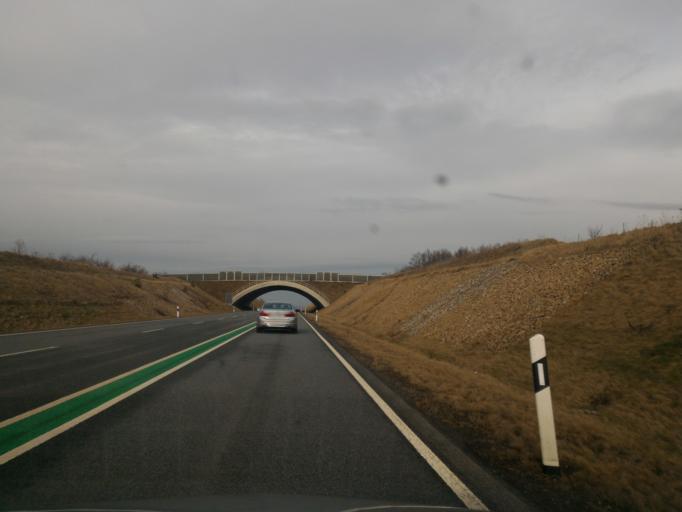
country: DE
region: Saxony
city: Niedercunnersdorf
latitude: 51.0491
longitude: 14.6750
